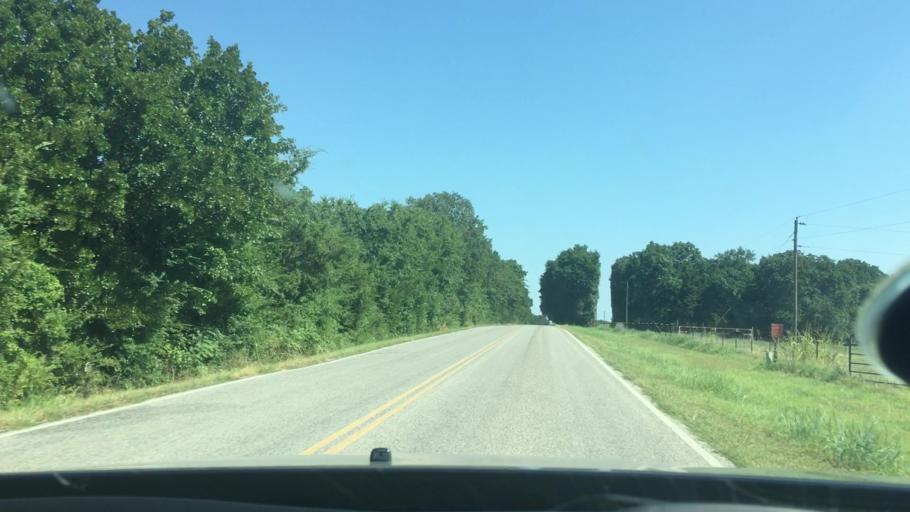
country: US
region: Oklahoma
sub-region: Johnston County
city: Tishomingo
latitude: 34.2944
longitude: -96.6185
